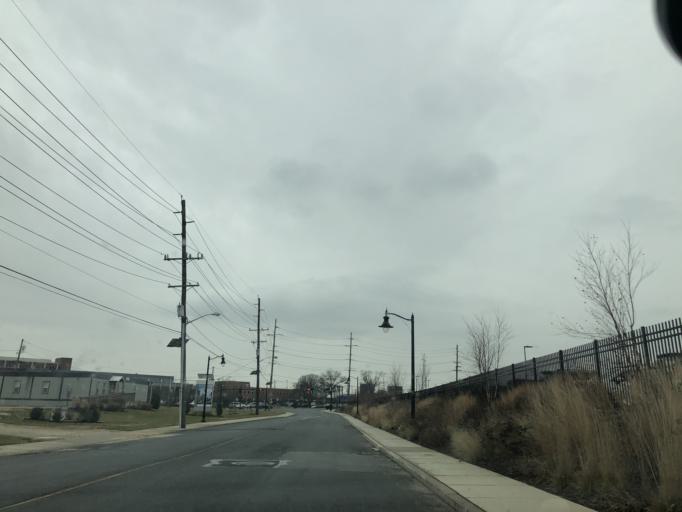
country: US
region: New Jersey
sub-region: Camden County
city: Camden
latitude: 39.9425
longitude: -75.1070
